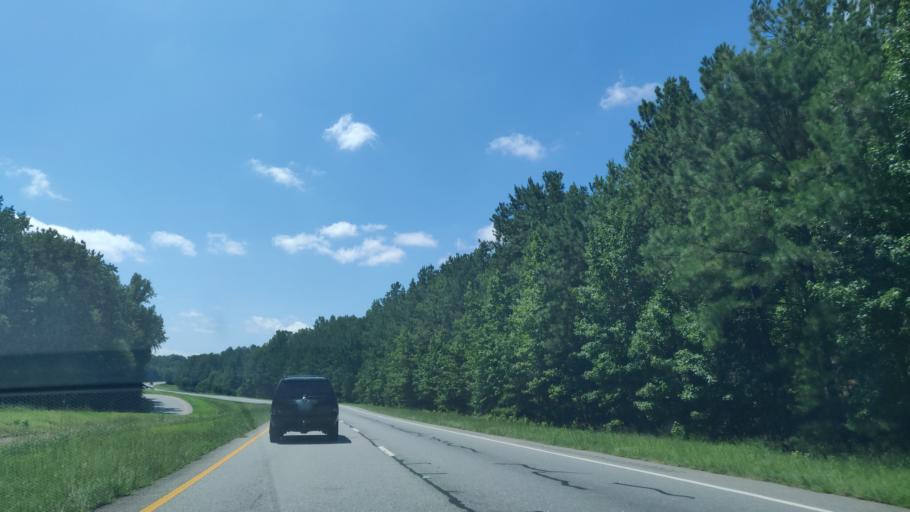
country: US
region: Georgia
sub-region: Chattahoochee County
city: Cusseta
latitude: 32.2444
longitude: -84.7187
